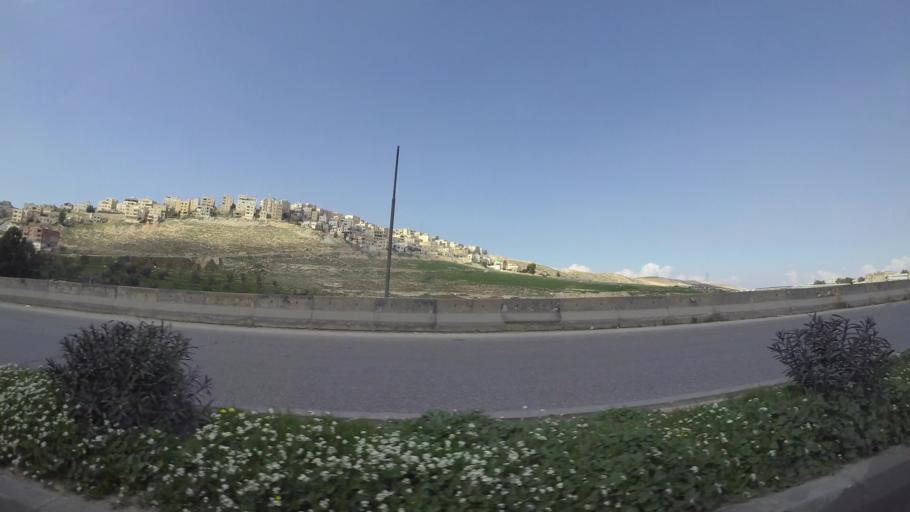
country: JO
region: Amman
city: Amman
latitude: 31.9920
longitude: 35.9828
